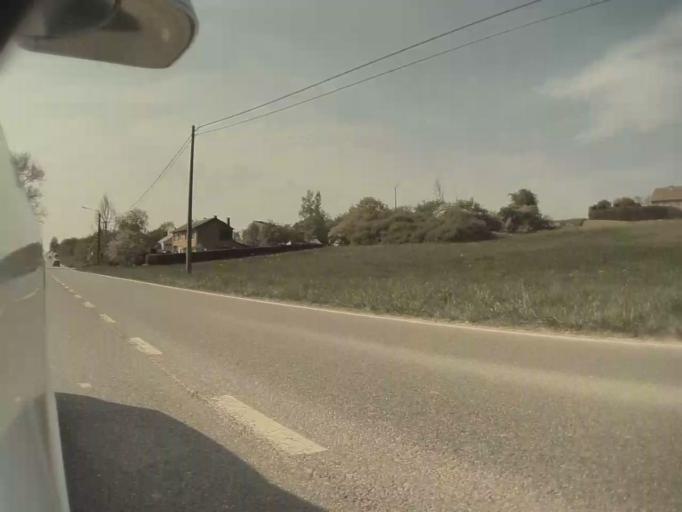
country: BE
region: Wallonia
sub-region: Province de Namur
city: Dinant
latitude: 50.2650
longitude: 4.9492
